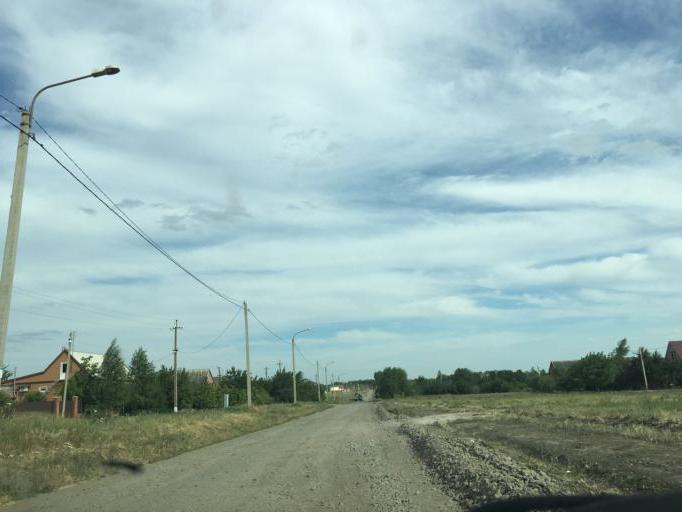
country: RU
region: Krasnodarskiy
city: Kushchevskaya
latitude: 46.5559
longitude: 39.6651
